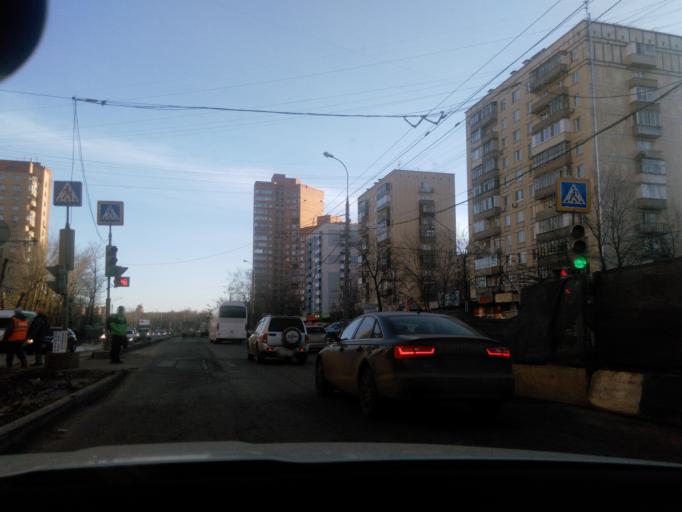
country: RU
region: Moskovskaya
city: Koptevo
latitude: 55.8232
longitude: 37.5277
